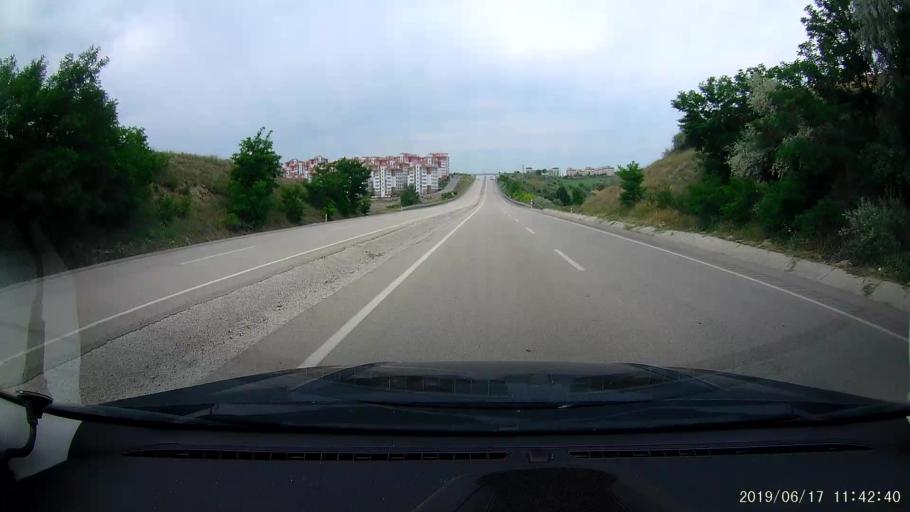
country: TR
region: Cankiri
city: Kursunlu
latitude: 40.8373
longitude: 33.2951
